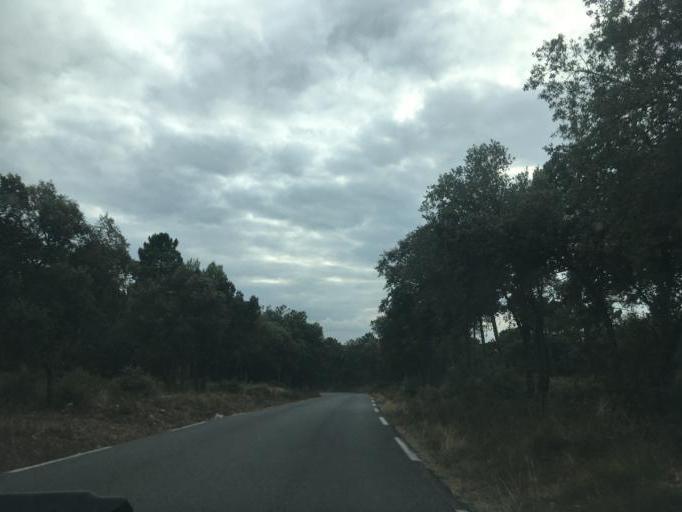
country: FR
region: Provence-Alpes-Cote d'Azur
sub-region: Departement du Var
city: Villecroze
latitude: 43.5535
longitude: 6.3285
